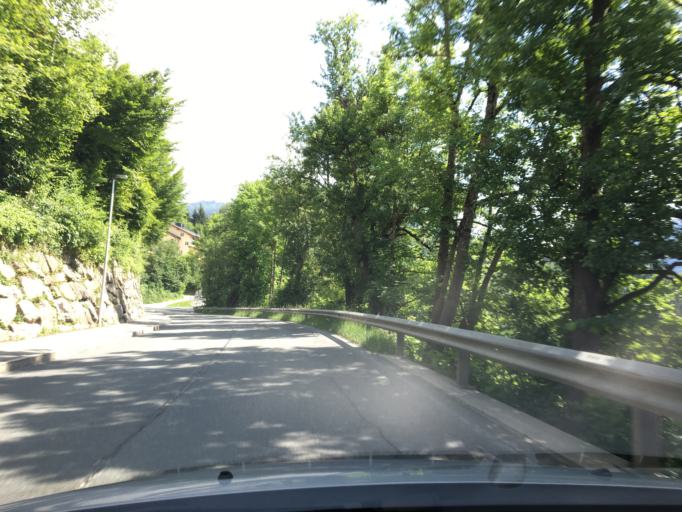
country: AT
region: Salzburg
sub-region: Politischer Bezirk Sankt Johann im Pongau
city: Sankt Johann im Pongau
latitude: 47.3459
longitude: 13.2068
